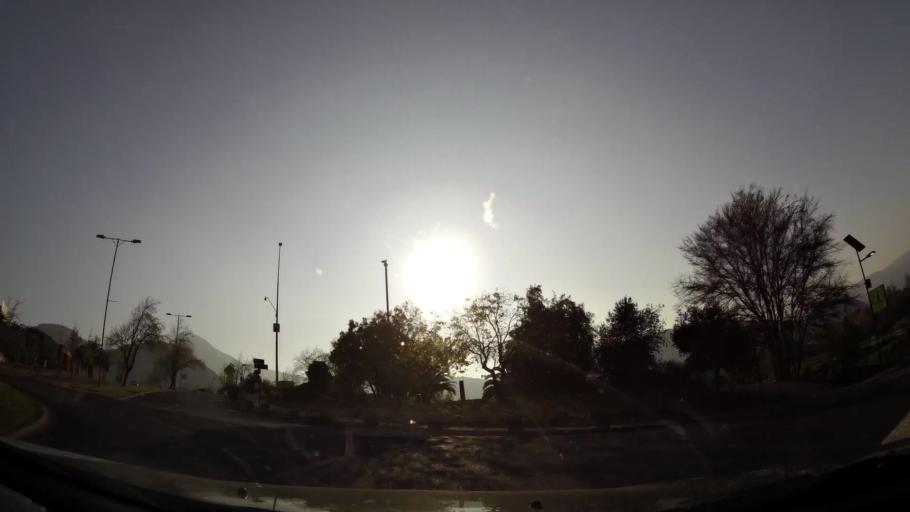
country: CL
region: Santiago Metropolitan
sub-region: Provincia de Chacabuco
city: Chicureo Abajo
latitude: -33.3425
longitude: -70.5462
